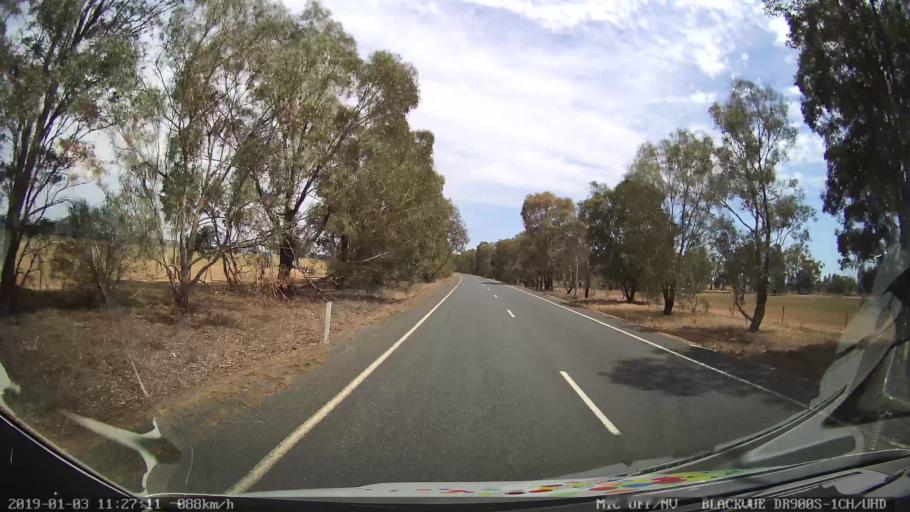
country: AU
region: New South Wales
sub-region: Weddin
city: Grenfell
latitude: -34.0156
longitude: 148.2207
